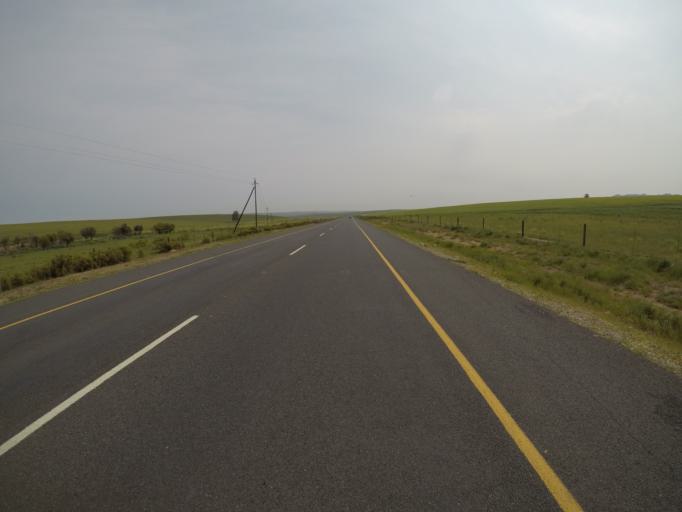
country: ZA
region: Western Cape
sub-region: West Coast District Municipality
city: Malmesbury
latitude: -33.4692
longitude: 18.7924
